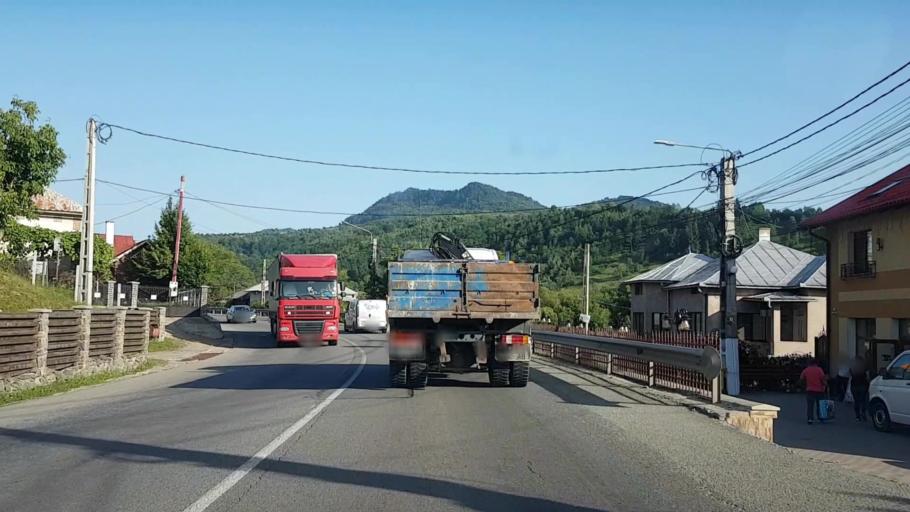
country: RO
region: Bistrita-Nasaud
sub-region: Comuna Tiha Bargaului
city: Tureac
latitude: 47.2284
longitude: 24.8056
